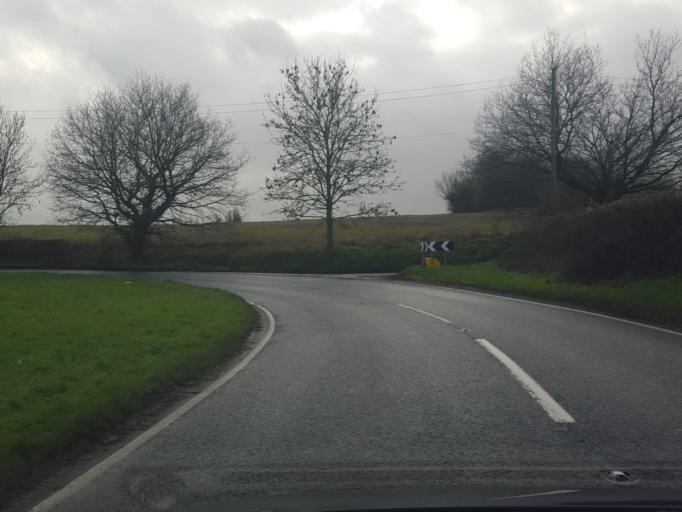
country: GB
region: England
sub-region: Essex
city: Eight Ash Green
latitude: 51.9593
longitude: 0.7851
